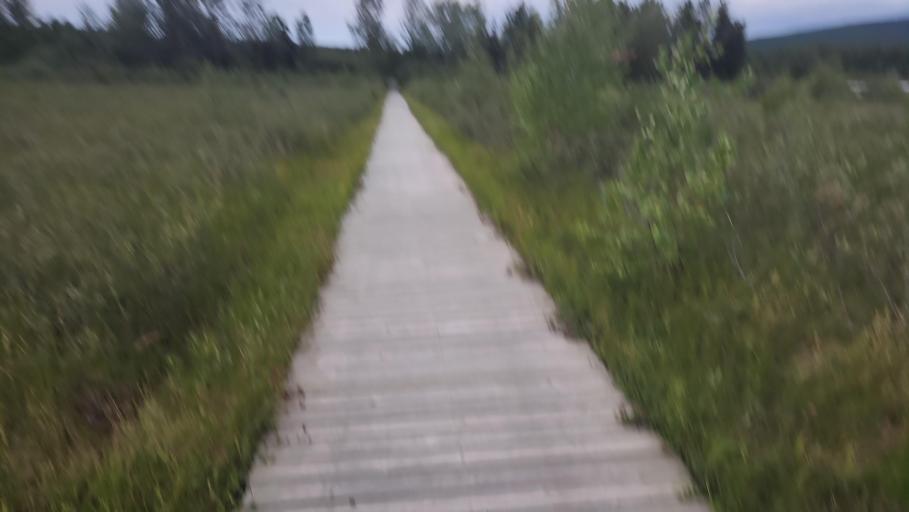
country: CA
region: Yukon
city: Watson Lake
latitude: 60.0645
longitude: -128.7047
